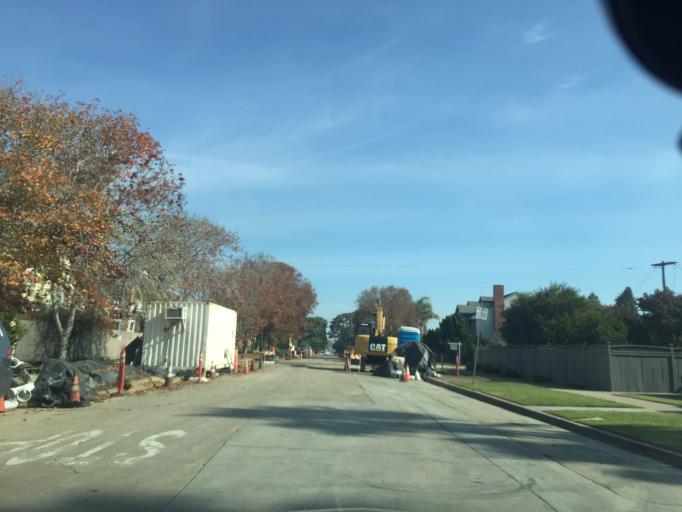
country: US
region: California
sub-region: San Diego County
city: La Jolla
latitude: 32.7922
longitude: -117.2521
